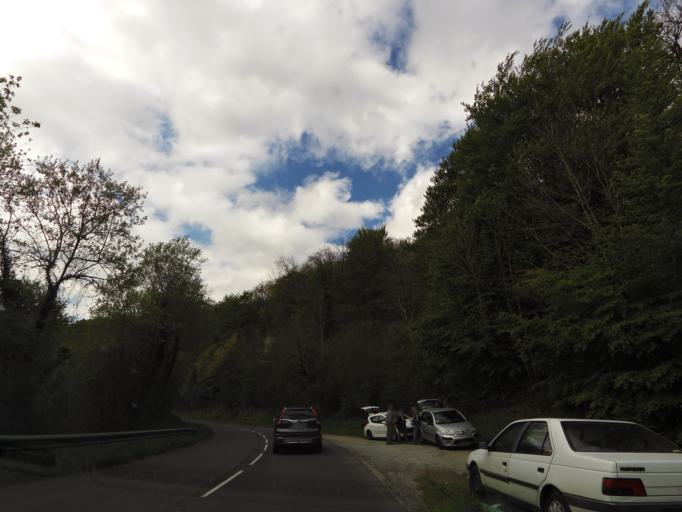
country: FR
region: Midi-Pyrenees
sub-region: Departement du Tarn
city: Soreze
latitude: 43.4182
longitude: 2.0614
